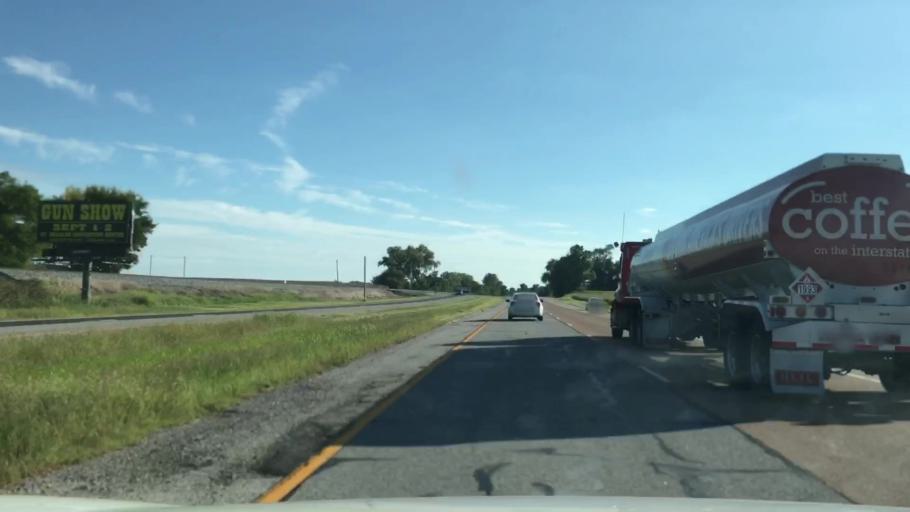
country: US
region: Illinois
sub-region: Madison County
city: Mitchell
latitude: 38.7901
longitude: -90.1050
